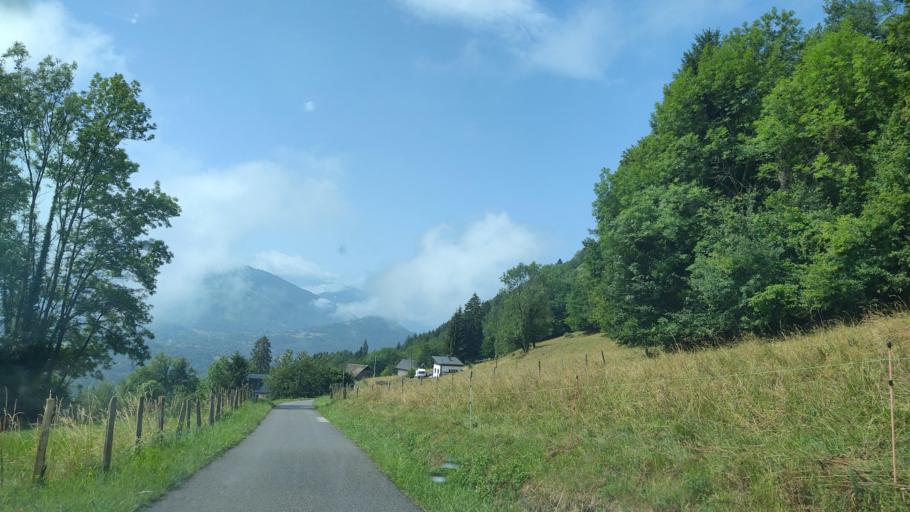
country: FR
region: Rhone-Alpes
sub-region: Departement de la Savoie
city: La Rochette
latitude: 45.4909
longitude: 6.1303
